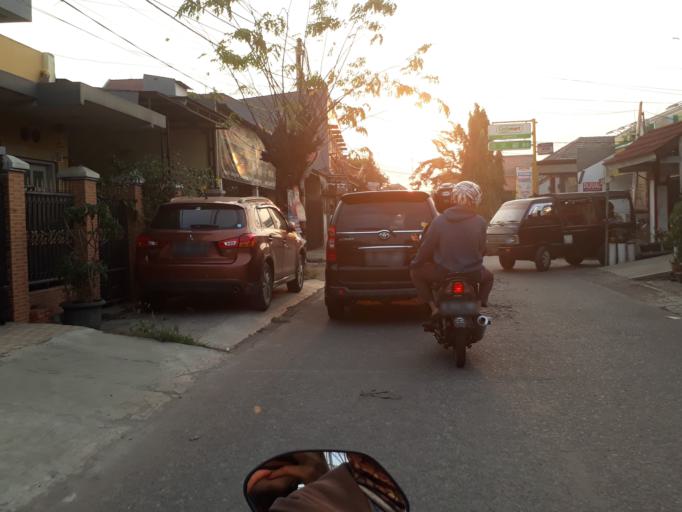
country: ID
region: West Java
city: Bekasi
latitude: -6.2400
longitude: 107.0372
